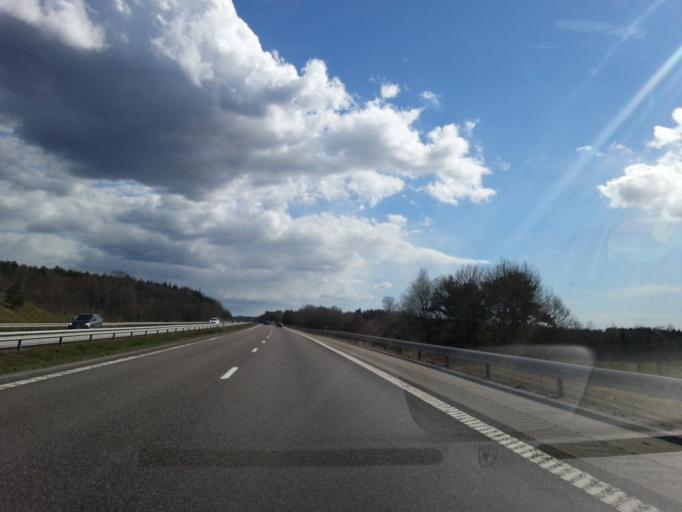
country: SE
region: Vaestra Goetaland
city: Svanesund
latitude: 58.0886
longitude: 11.8827
